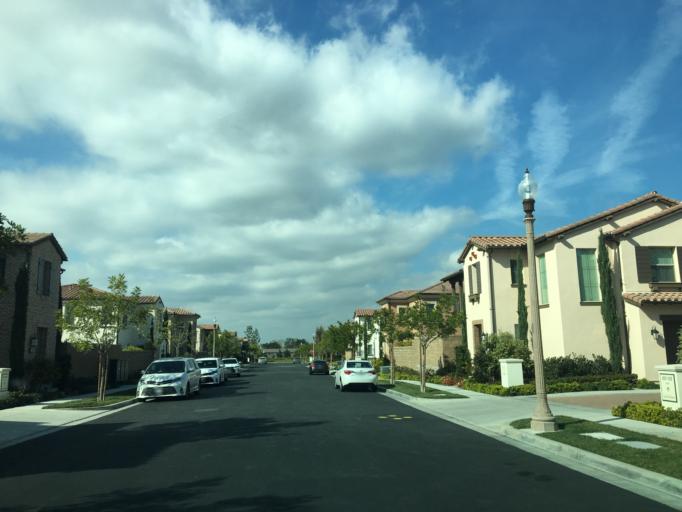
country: US
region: California
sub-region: Orange County
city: North Tustin
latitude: 33.7108
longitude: -117.7544
